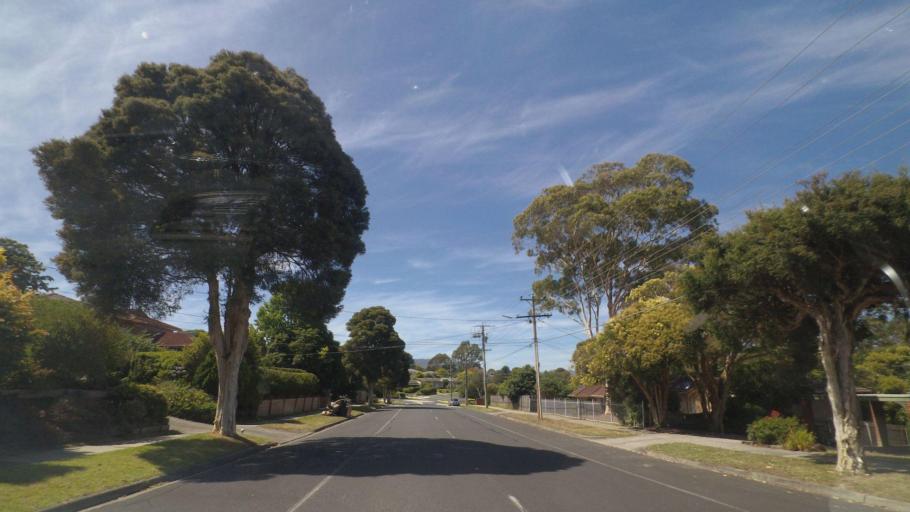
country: AU
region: Victoria
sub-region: Maroondah
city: Croydon North
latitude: -37.7765
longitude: 145.3081
